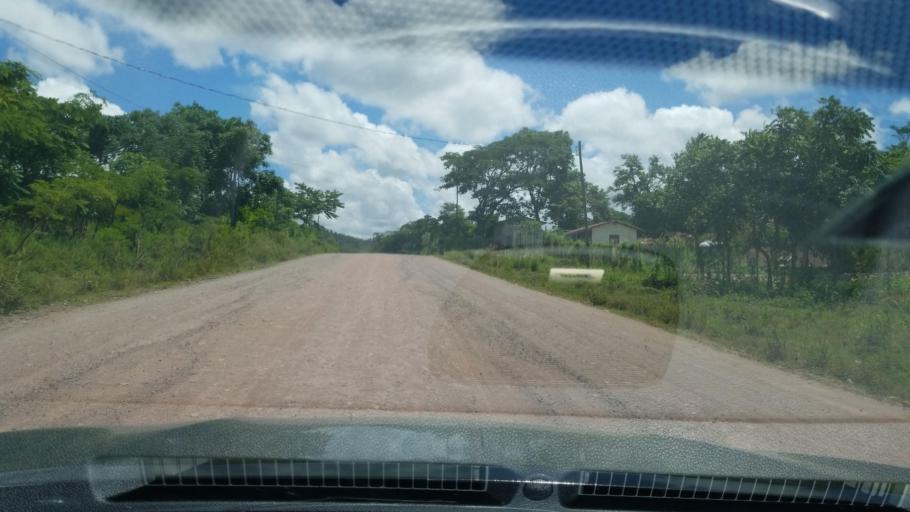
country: HN
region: Francisco Morazan
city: San Juan de Flores
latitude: 14.3264
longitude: -87.0466
